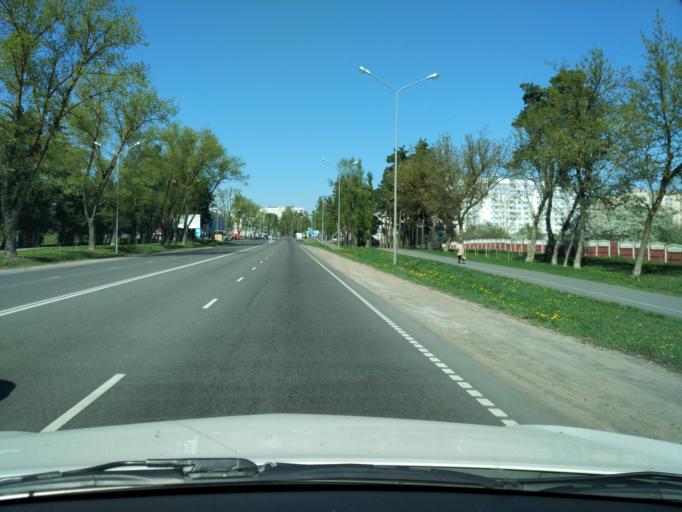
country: BY
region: Minsk
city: Borovlyany
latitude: 53.9977
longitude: 27.6749
